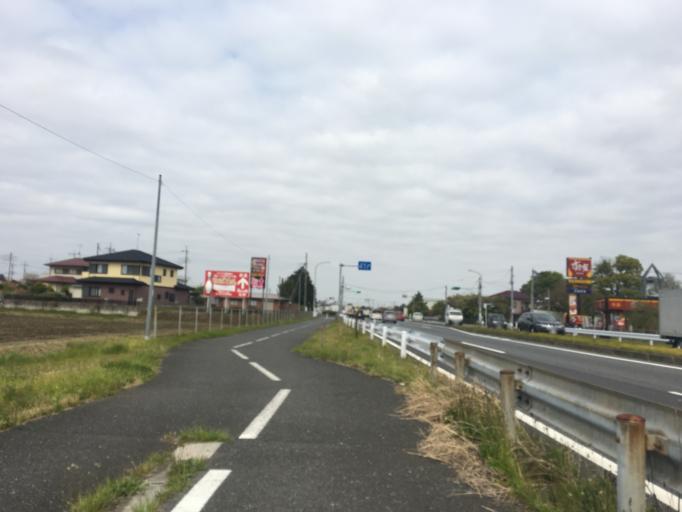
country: JP
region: Saitama
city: Shiki
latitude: 35.8506
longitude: 139.5684
